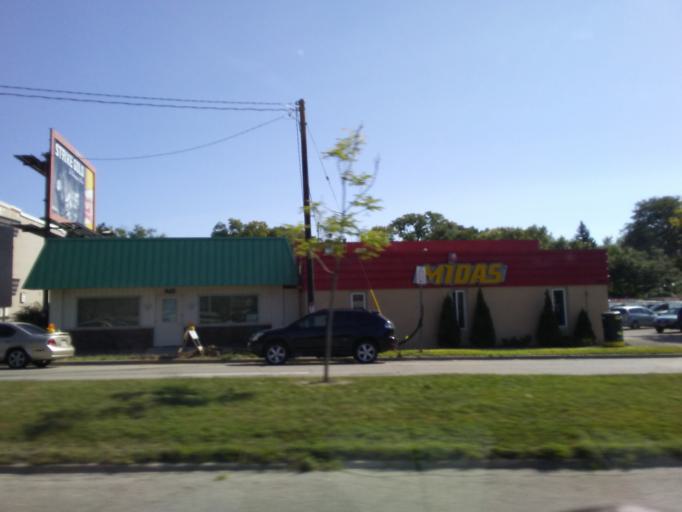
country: US
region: Wisconsin
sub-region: Dane County
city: Madison
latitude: 43.0505
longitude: -89.3944
